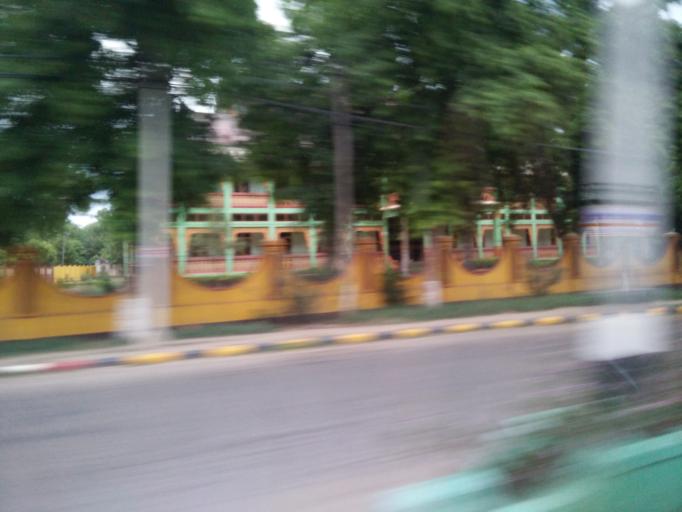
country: MM
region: Magway
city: Pakokku
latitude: 21.3312
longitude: 95.0715
